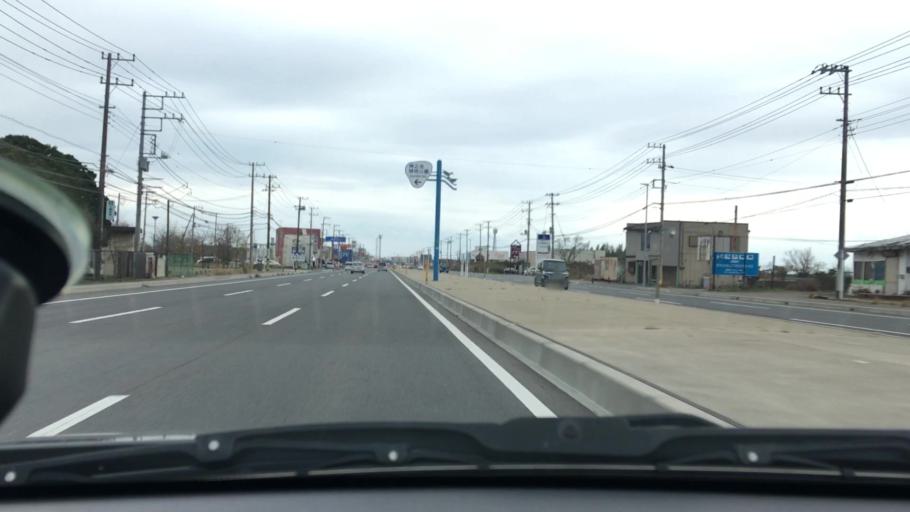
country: JP
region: Chiba
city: Omigawa
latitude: 35.8868
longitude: 140.6702
